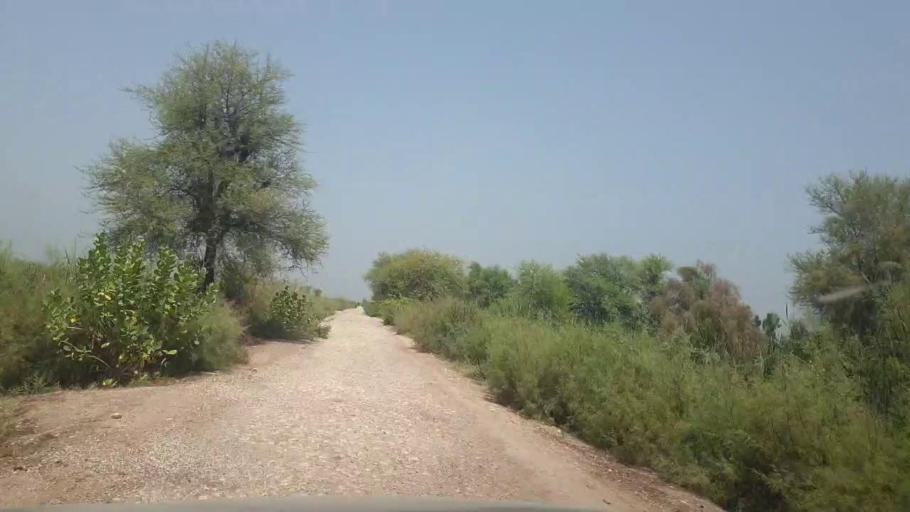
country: PK
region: Sindh
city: Lakhi
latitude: 27.8372
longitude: 68.6252
